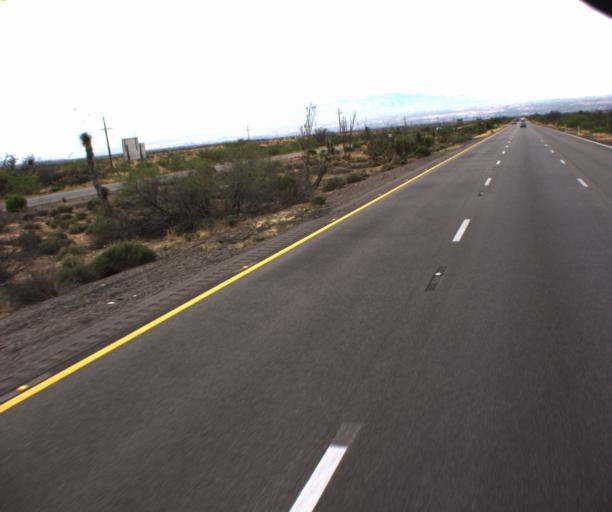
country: US
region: Arizona
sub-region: Cochise County
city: Saint David
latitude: 31.9917
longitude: -110.1792
